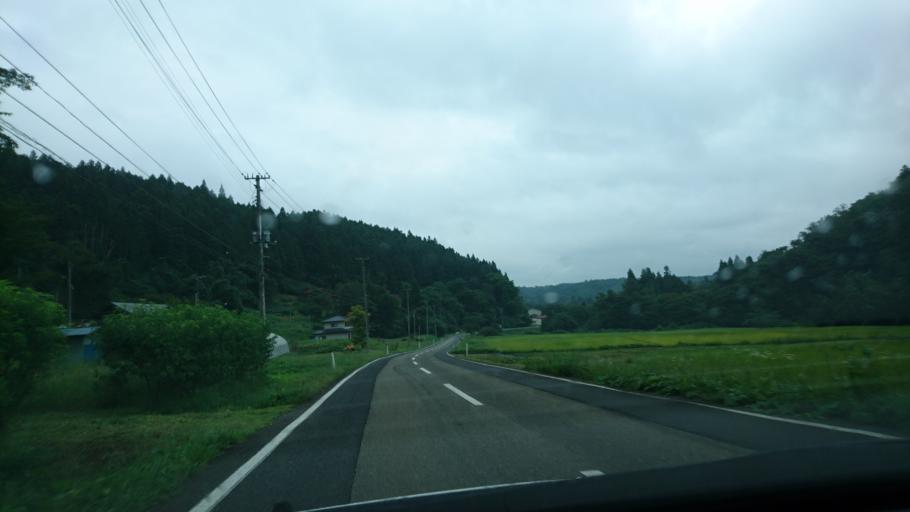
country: JP
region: Iwate
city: Ichinoseki
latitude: 38.9031
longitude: 141.0433
